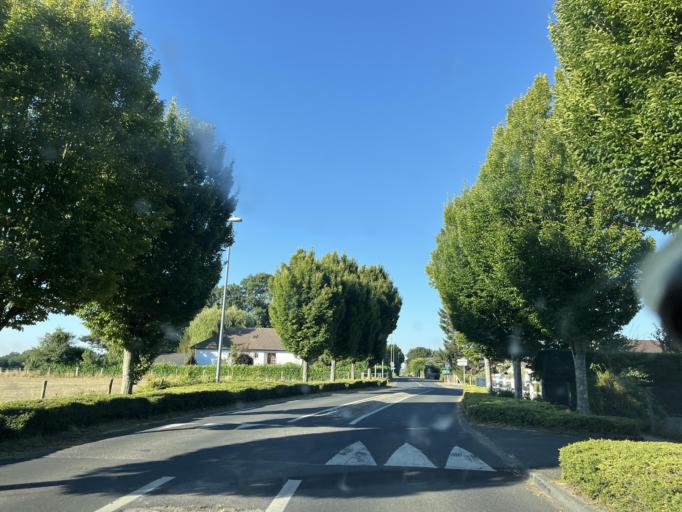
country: FR
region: Haute-Normandie
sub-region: Departement de la Seine-Maritime
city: Lillebonne
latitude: 49.5434
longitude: 0.5571
